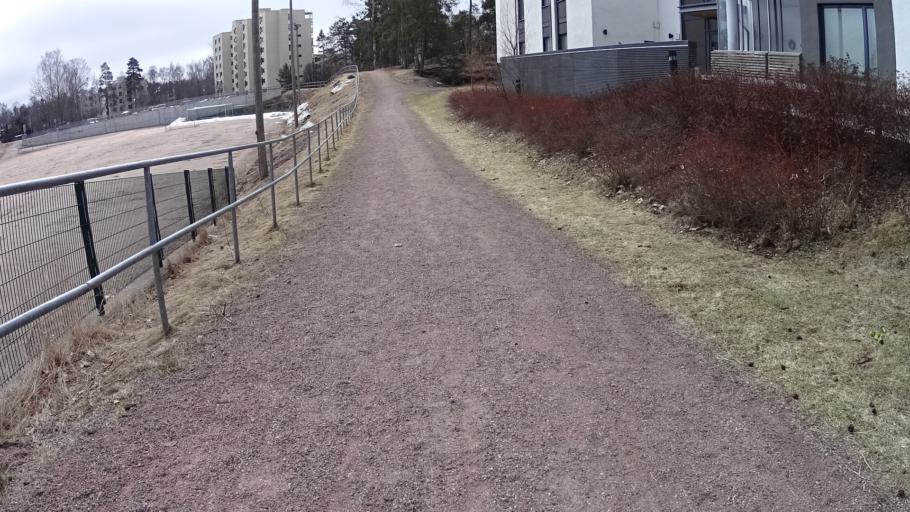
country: FI
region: Uusimaa
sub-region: Helsinki
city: Koukkuniemi
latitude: 60.1655
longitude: 24.7774
